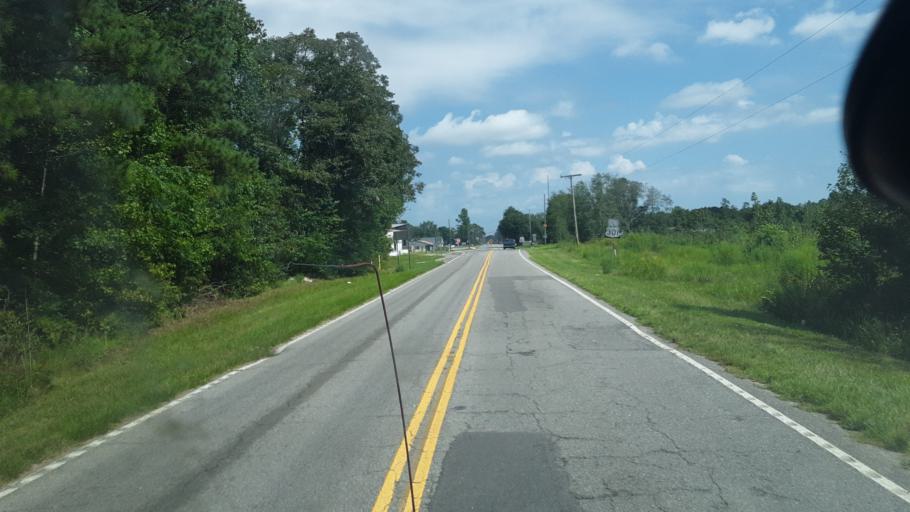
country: US
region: South Carolina
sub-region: Bamberg County
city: Bamberg
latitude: 33.2830
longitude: -81.0403
